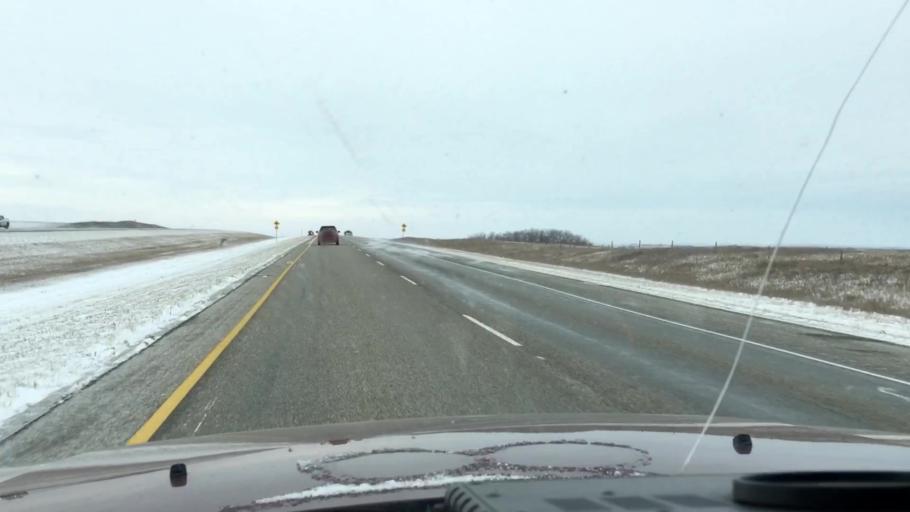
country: CA
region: Saskatchewan
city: Saskatoon
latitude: 51.6716
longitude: -106.4492
